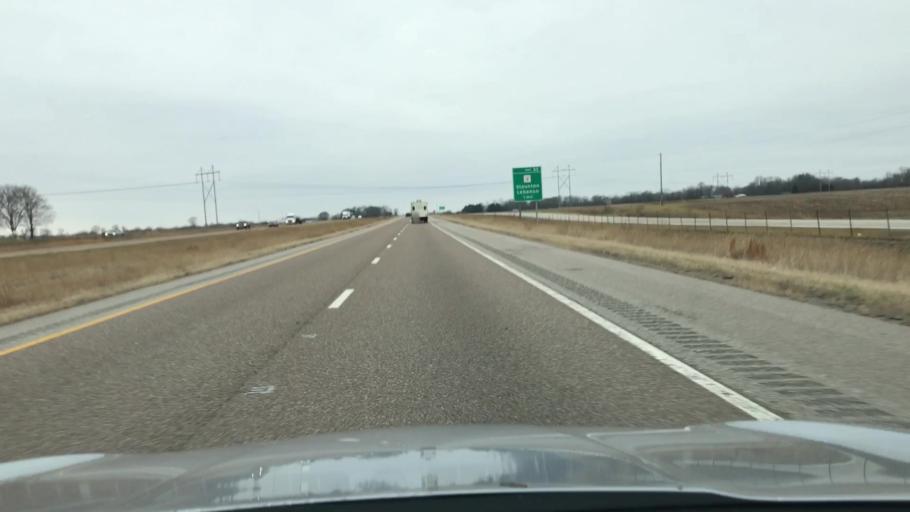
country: US
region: Illinois
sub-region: Madison County
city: Worden
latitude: 38.9459
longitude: -89.7825
